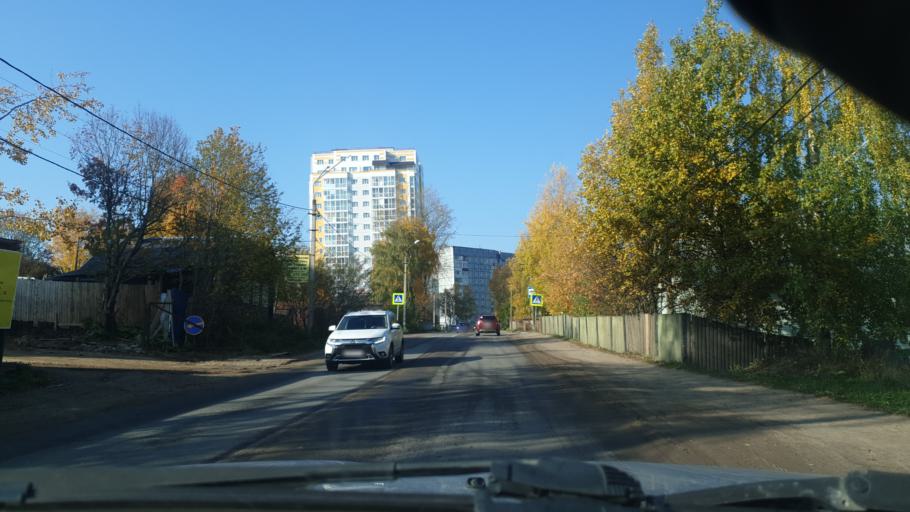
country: RU
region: Komi Republic
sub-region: Syktyvdinskiy Rayon
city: Syktyvkar
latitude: 61.6909
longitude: 50.8267
